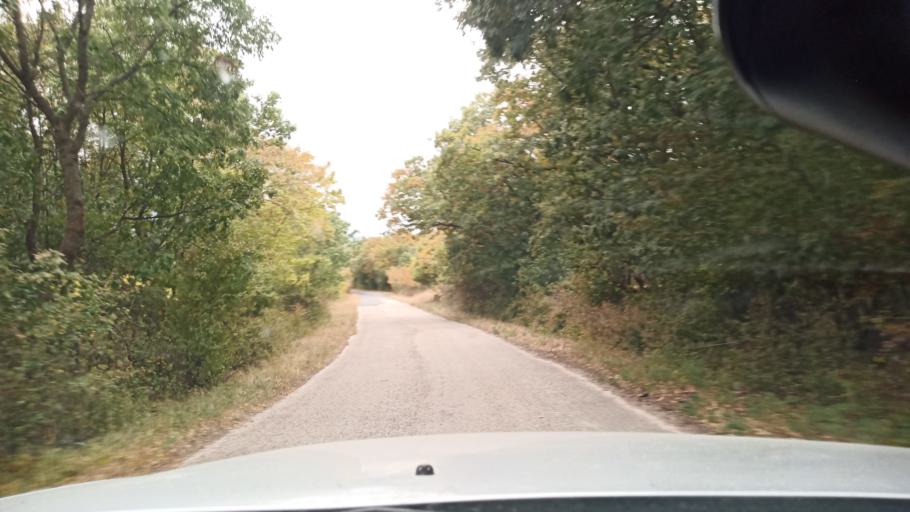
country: HU
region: Fejer
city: Zamoly
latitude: 47.3533
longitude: 18.3435
